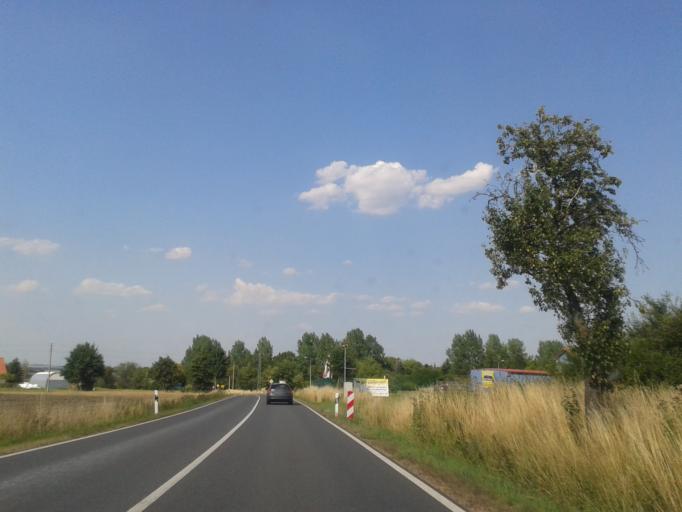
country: DE
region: Saxony
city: Niederschona
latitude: 50.9930
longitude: 13.4522
